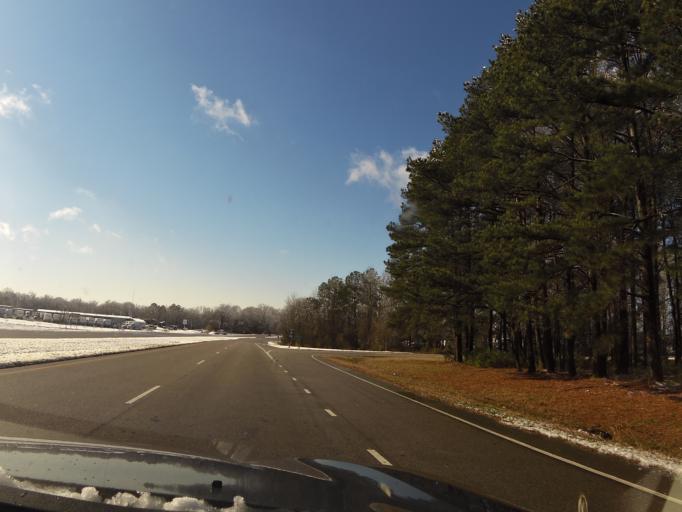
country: US
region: North Carolina
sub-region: Wilson County
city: Wilson
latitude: 35.7352
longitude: -77.8794
